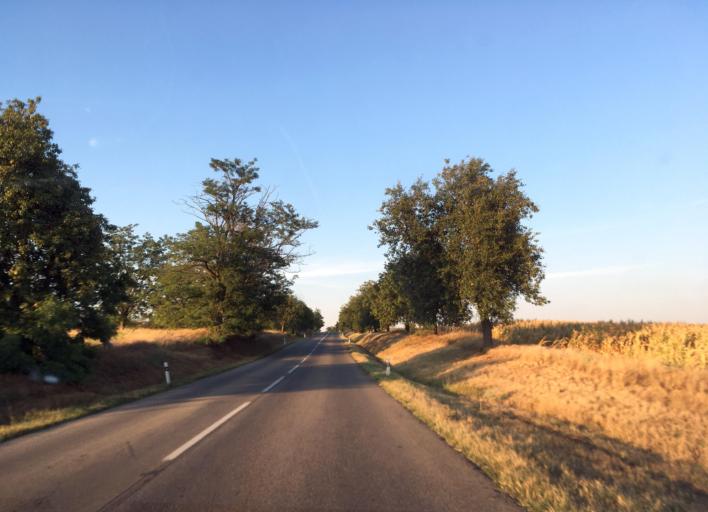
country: HU
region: Komarom-Esztergom
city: Neszmely
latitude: 47.8104
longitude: 18.3390
